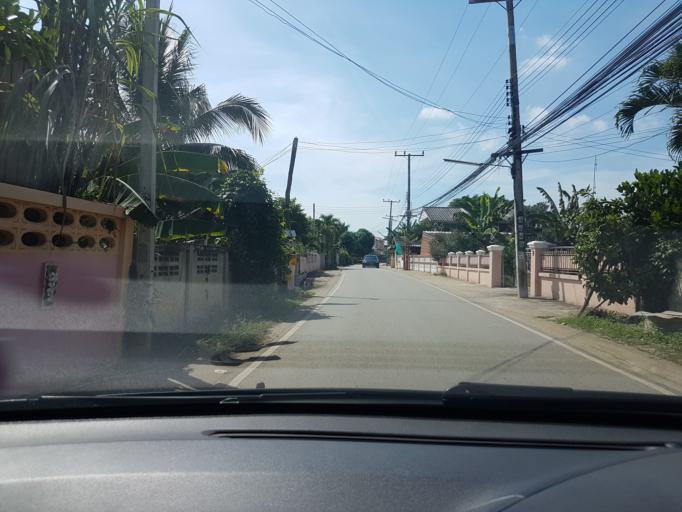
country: TH
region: Lampang
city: Ko Kha
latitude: 18.2179
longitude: 99.4134
